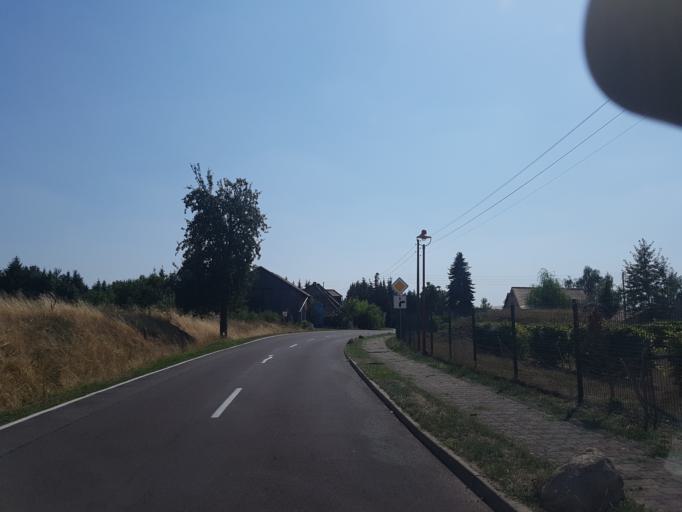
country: DE
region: Saxony-Anhalt
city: Klieken
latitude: 52.0095
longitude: 12.3802
